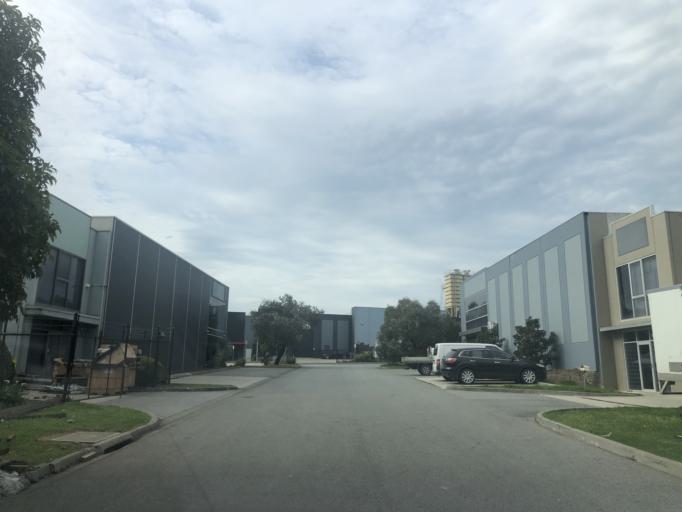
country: AU
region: Victoria
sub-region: Casey
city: Hallam
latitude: -38.0157
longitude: 145.2584
